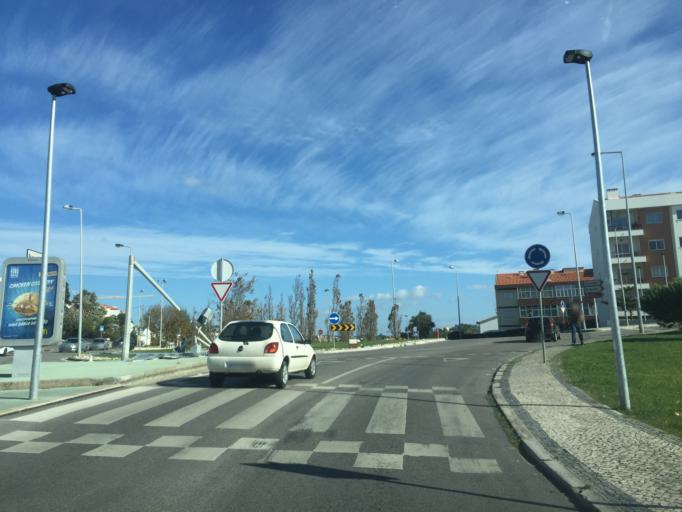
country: PT
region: Coimbra
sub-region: Figueira da Foz
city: Tavarede
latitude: 40.1645
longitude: -8.8523
